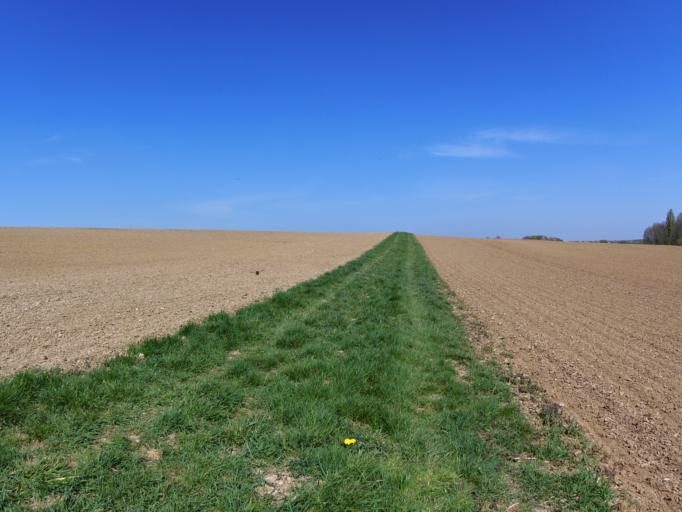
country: DE
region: Bavaria
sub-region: Regierungsbezirk Unterfranken
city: Giebelstadt
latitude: 49.6919
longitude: 9.9597
